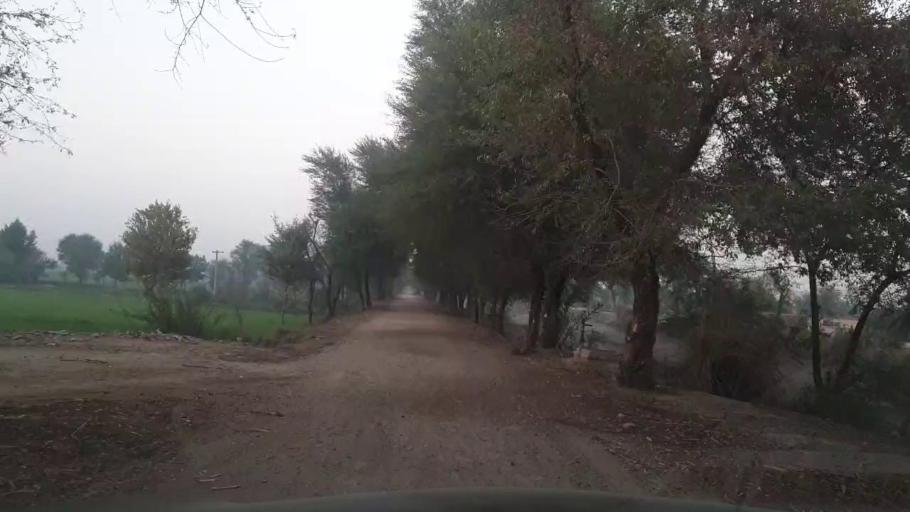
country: PK
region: Sindh
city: Ubauro
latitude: 28.1773
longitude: 69.7798
